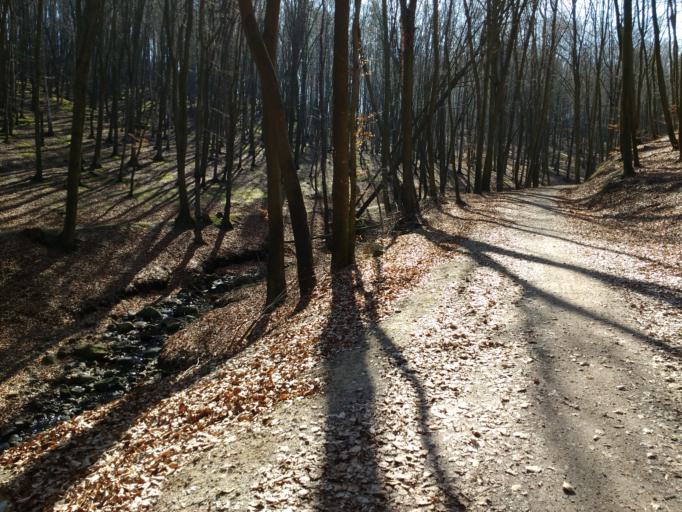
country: PL
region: Pomeranian Voivodeship
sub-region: Gdynia
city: Wielki Kack
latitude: 54.4809
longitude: 18.5151
